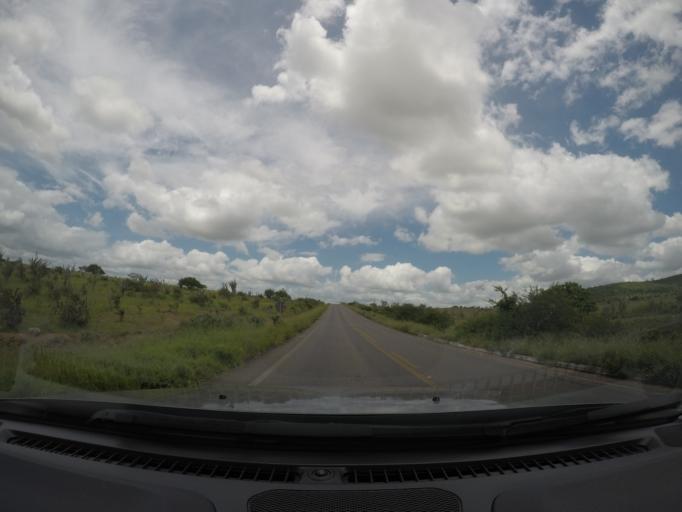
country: BR
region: Bahia
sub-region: Ipira
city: Ipira
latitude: -12.2636
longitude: -39.8309
